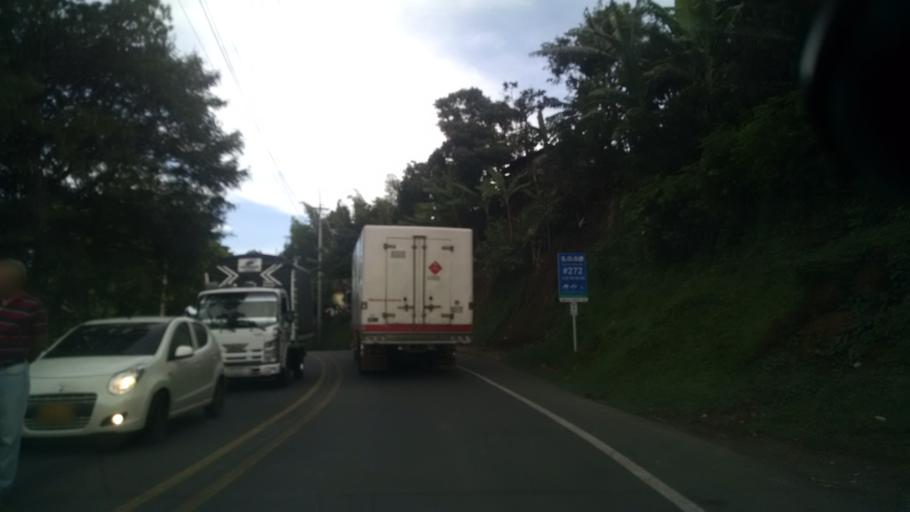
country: CO
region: Antioquia
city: Santa Barbara
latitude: 5.8802
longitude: -75.5701
